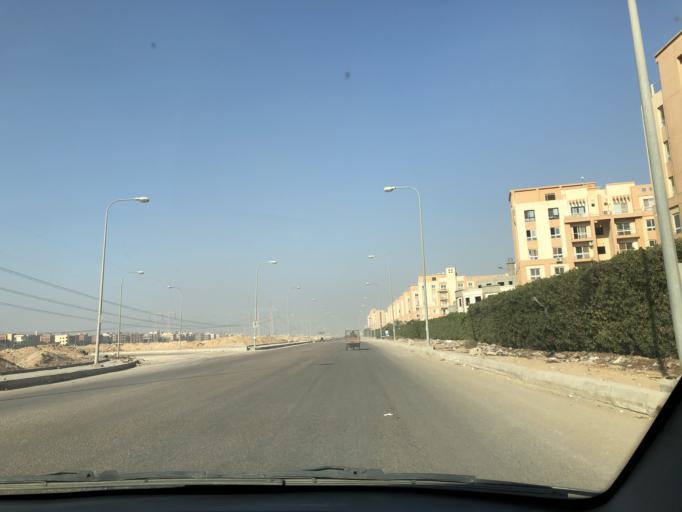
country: EG
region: Al Jizah
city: Madinat Sittah Uktubar
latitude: 29.9102
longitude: 31.0518
